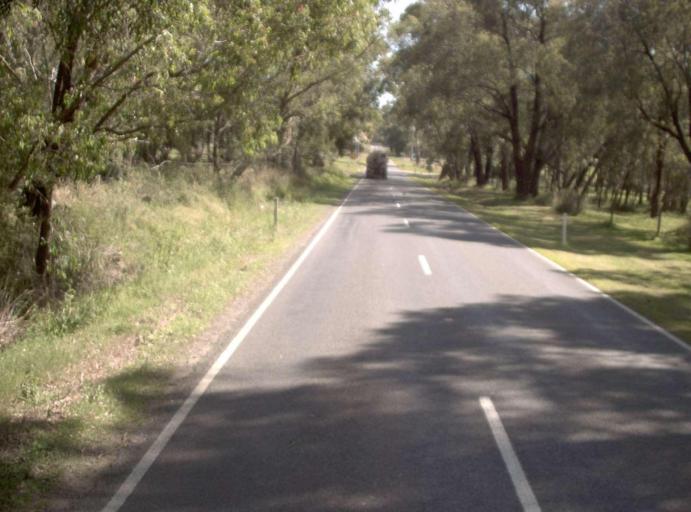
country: AU
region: Victoria
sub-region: Cardinia
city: Bunyip
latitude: -38.2389
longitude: 145.7808
